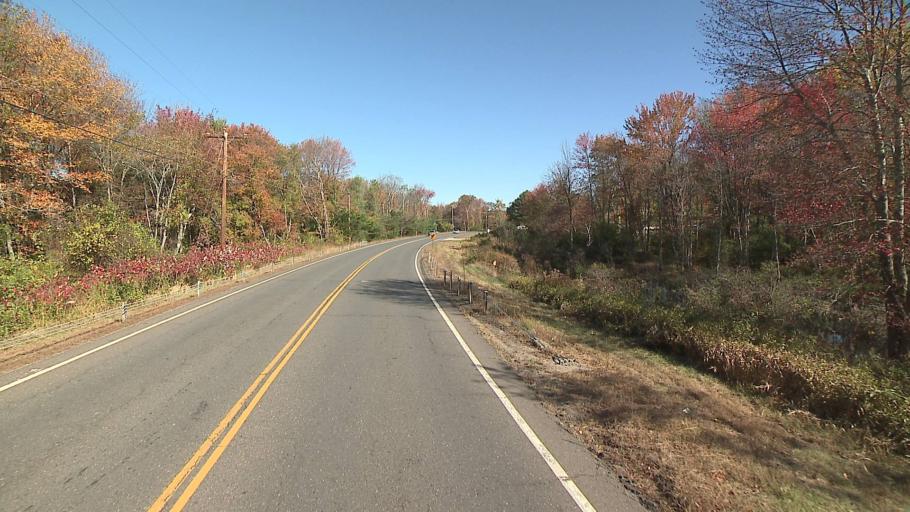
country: US
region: Connecticut
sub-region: Tolland County
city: South Coventry
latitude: 41.7153
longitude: -72.2841
